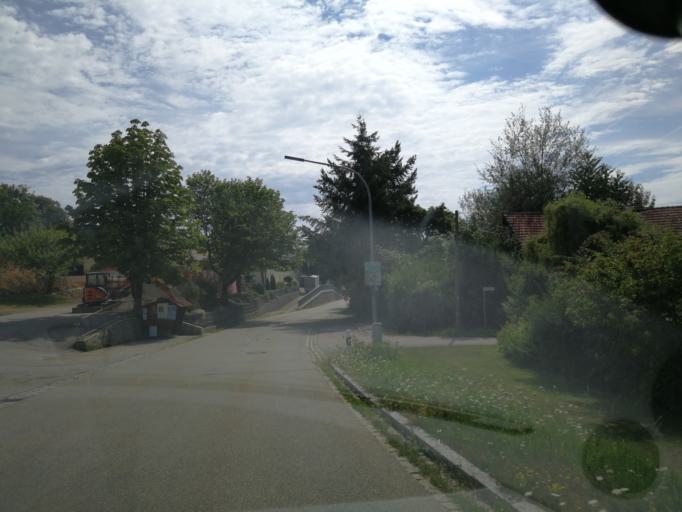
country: DE
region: Bavaria
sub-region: Upper Palatinate
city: Falkenstein
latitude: 49.0900
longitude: 12.4990
